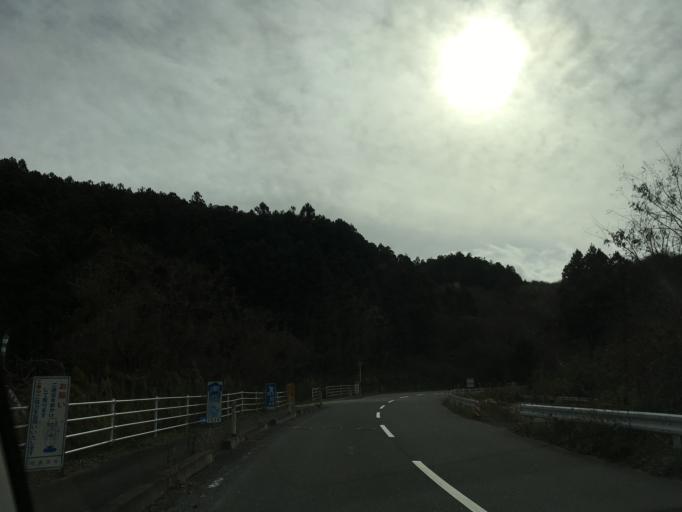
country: JP
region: Iwate
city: Ichinoseki
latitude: 38.7515
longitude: 141.2858
